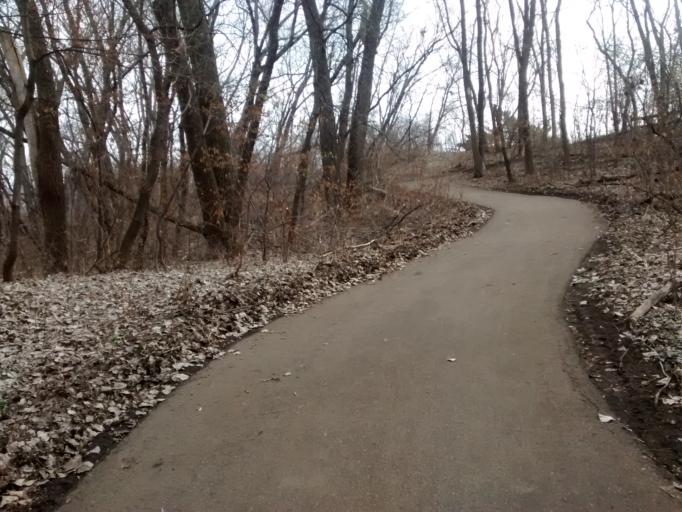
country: US
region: Minnesota
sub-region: Dakota County
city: Burnsville
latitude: 44.7607
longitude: -93.2980
